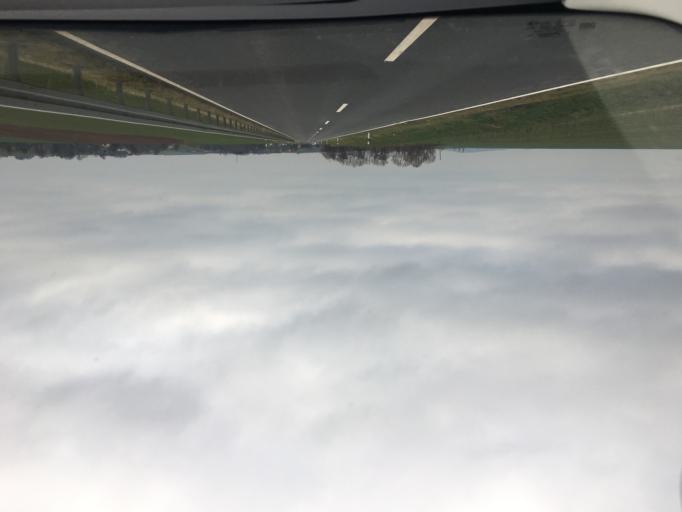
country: DE
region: Saxony
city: Niederfrohna
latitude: 50.8865
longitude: 12.7123
